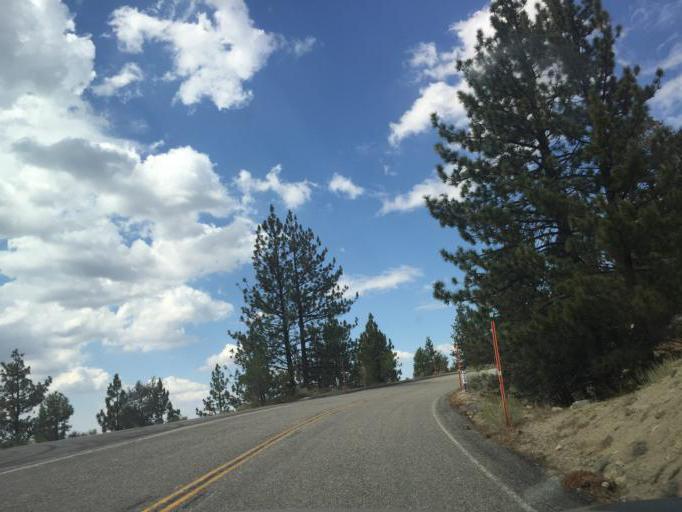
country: US
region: California
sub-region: Los Angeles County
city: Littlerock
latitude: 34.3525
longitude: -117.9462
